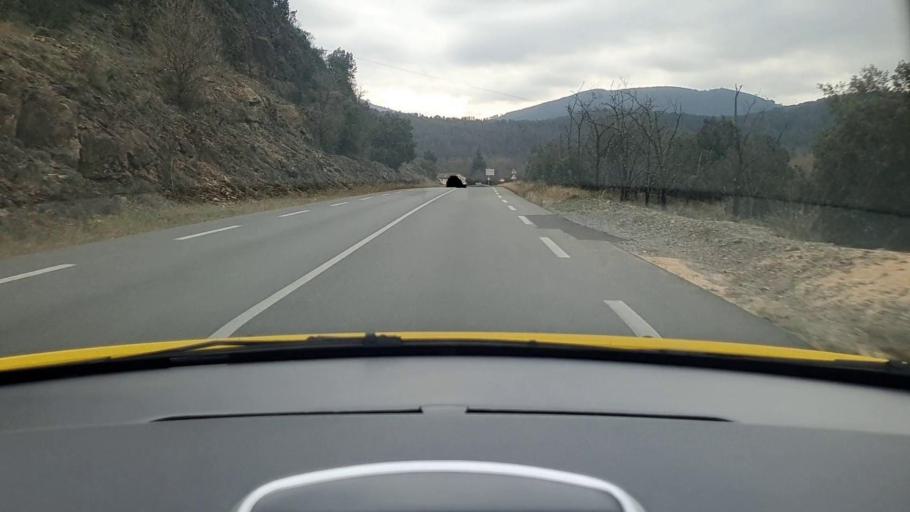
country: FR
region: Languedoc-Roussillon
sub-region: Departement du Gard
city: Besseges
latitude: 44.2810
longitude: 4.1285
